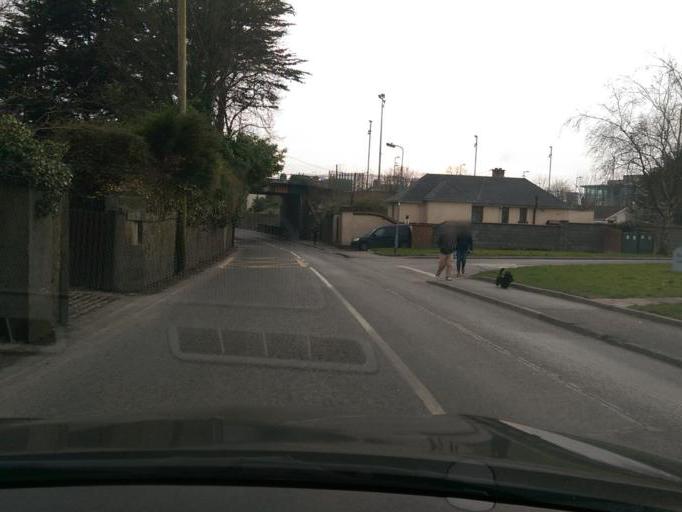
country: IE
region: Leinster
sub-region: An Iarmhi
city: Athlone
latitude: 53.4270
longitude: -7.9331
